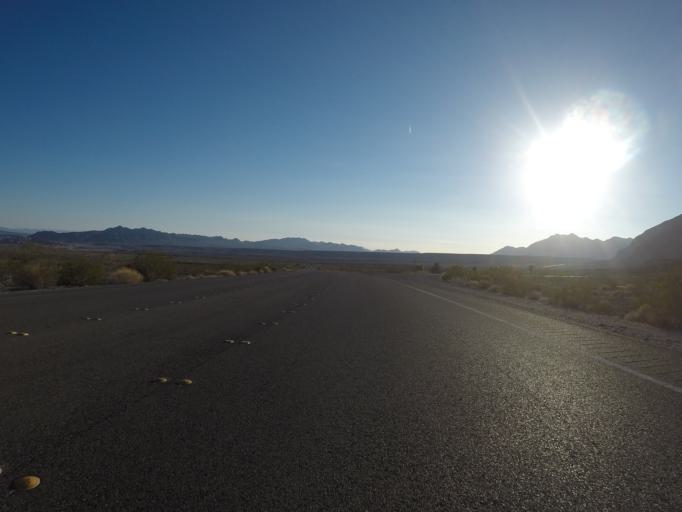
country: US
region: Nevada
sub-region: Clark County
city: Moapa Valley
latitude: 36.3780
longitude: -114.4409
